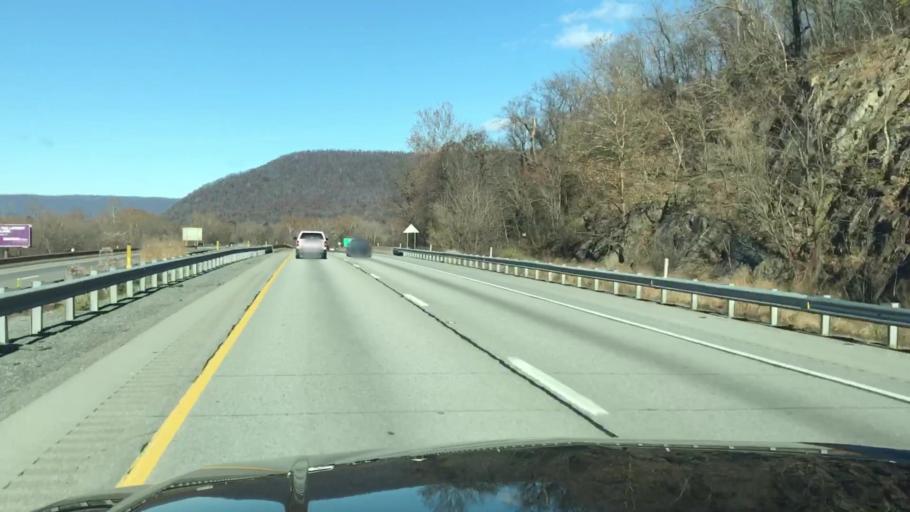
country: US
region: Pennsylvania
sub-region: Perry County
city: Marysville
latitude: 40.3386
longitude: -76.9038
